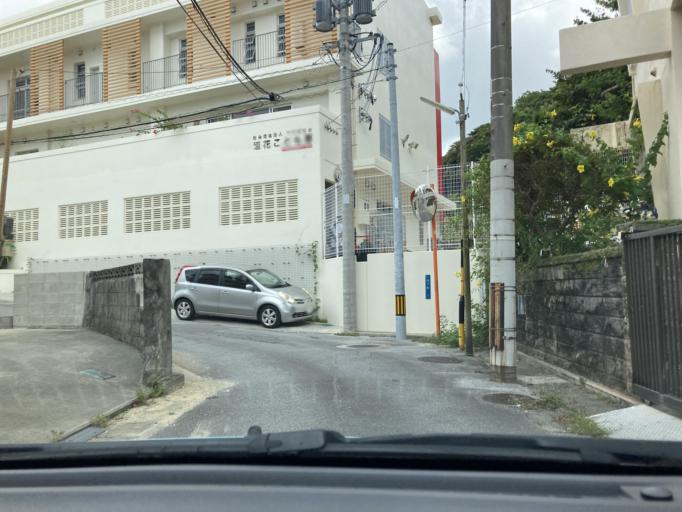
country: JP
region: Okinawa
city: Naha-shi
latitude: 26.2023
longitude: 127.6697
